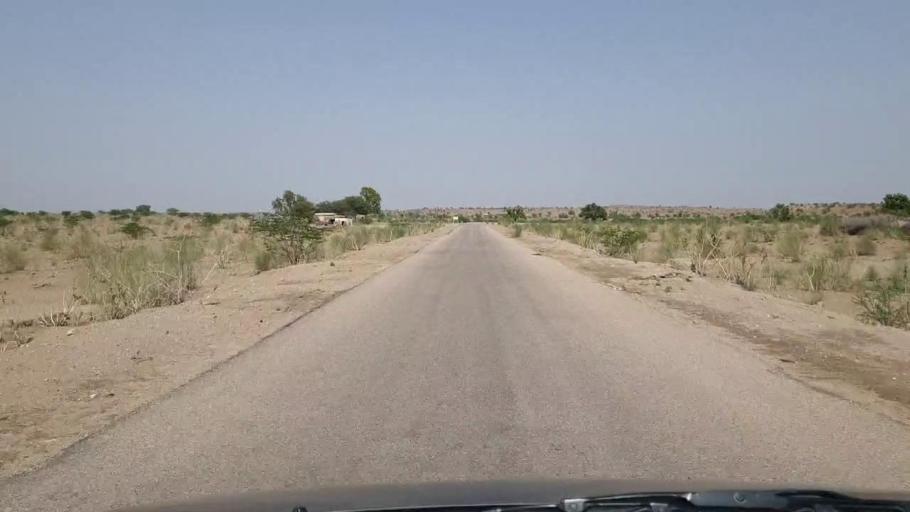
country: PK
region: Sindh
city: Chor
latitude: 25.4740
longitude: 70.5108
